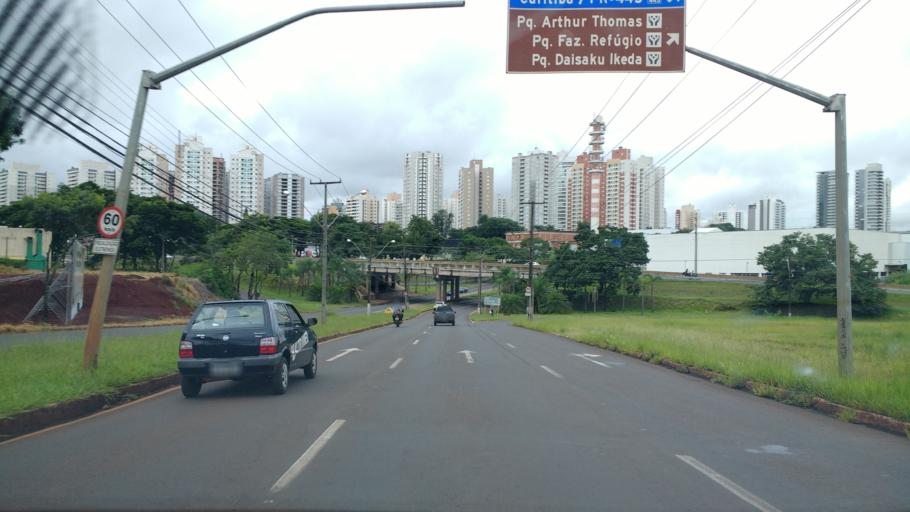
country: BR
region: Parana
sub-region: Londrina
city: Londrina
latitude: -23.3380
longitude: -51.1850
